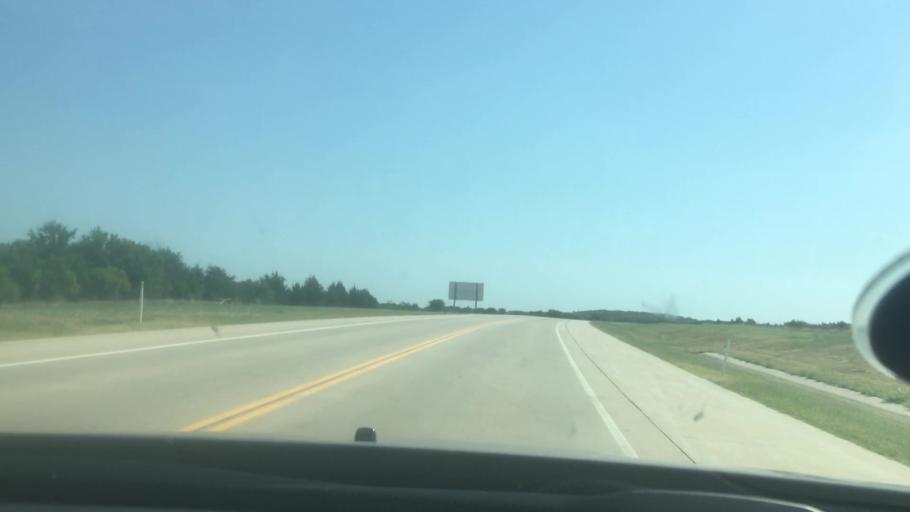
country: US
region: Oklahoma
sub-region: Murray County
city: Sulphur
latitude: 34.5802
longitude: -96.9218
